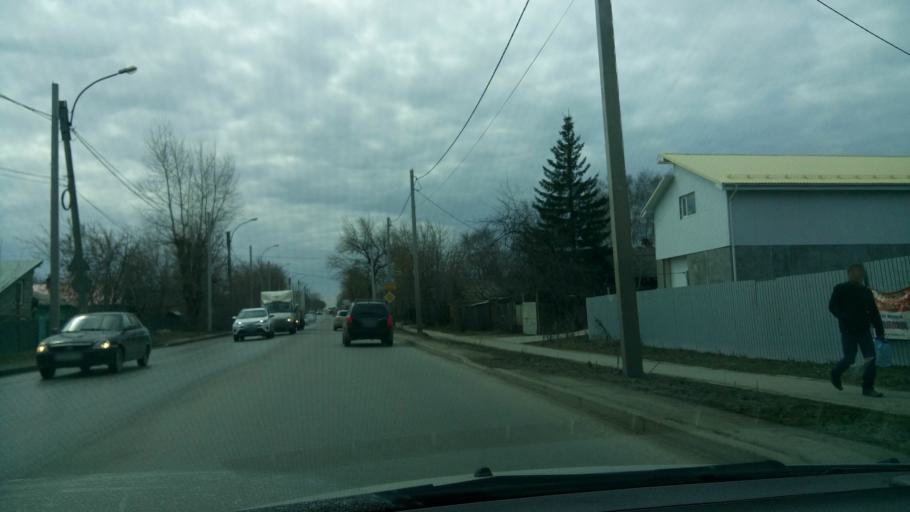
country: RU
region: Sverdlovsk
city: Yekaterinburg
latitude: 56.8718
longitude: 60.6842
